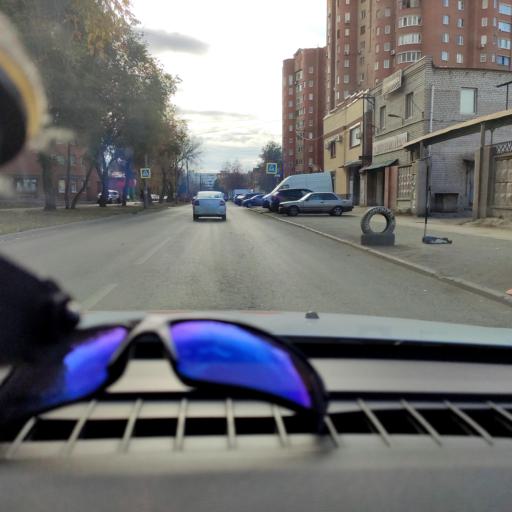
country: RU
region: Samara
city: Samara
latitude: 53.2482
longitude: 50.2104
